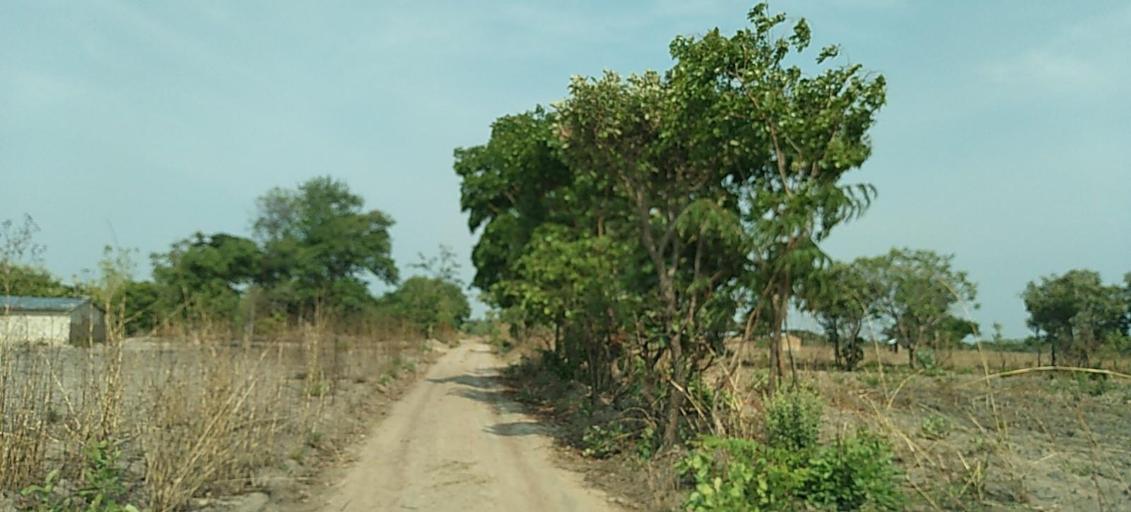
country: ZM
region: Copperbelt
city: Luanshya
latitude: -13.2168
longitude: 28.6470
